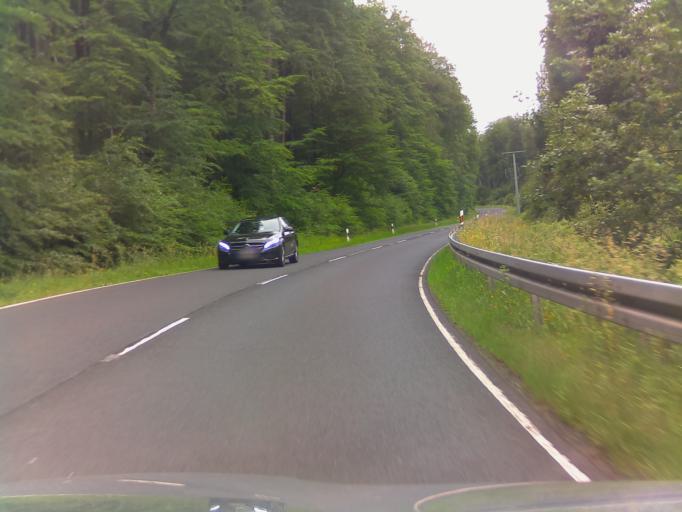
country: DE
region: Bavaria
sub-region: Regierungsbezirk Unterfranken
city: Weibersbrunn
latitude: 49.9386
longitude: 9.3391
